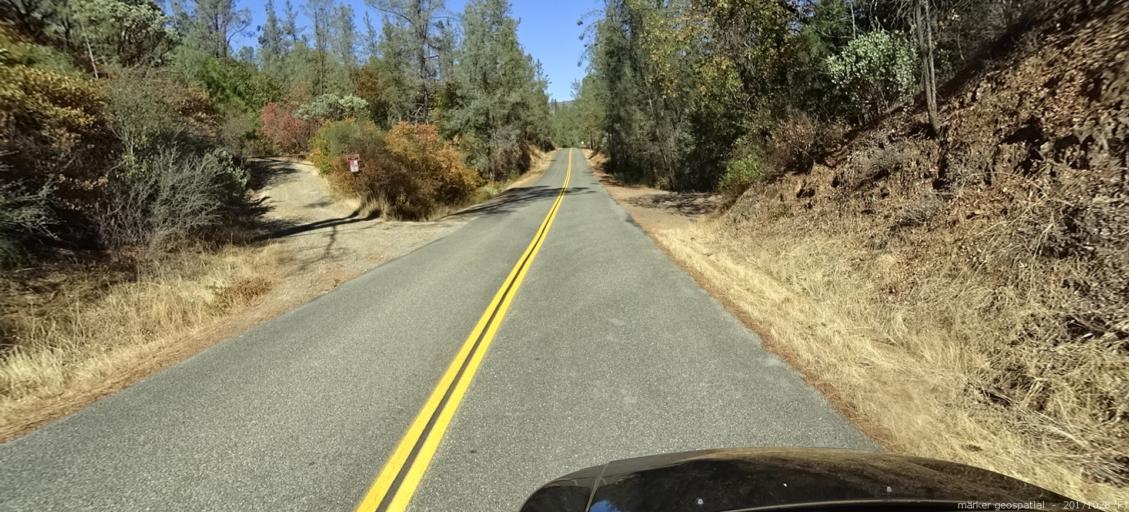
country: US
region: California
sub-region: Shasta County
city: Shasta
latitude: 40.6446
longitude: -122.5574
